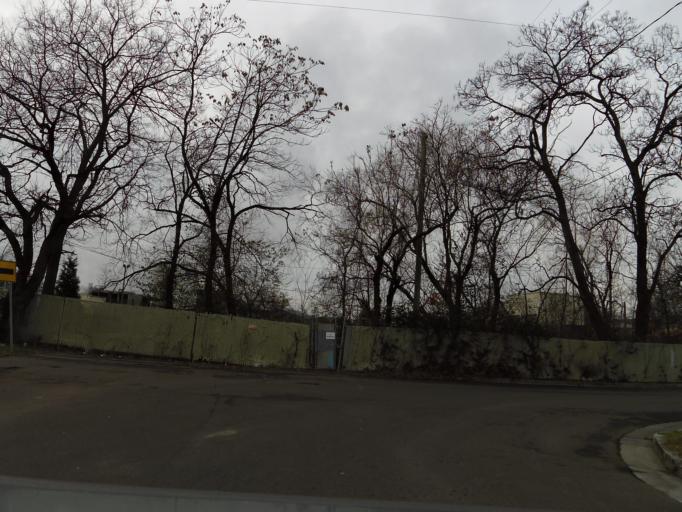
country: US
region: Tennessee
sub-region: Knox County
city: Knoxville
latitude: 35.9809
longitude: -83.9555
